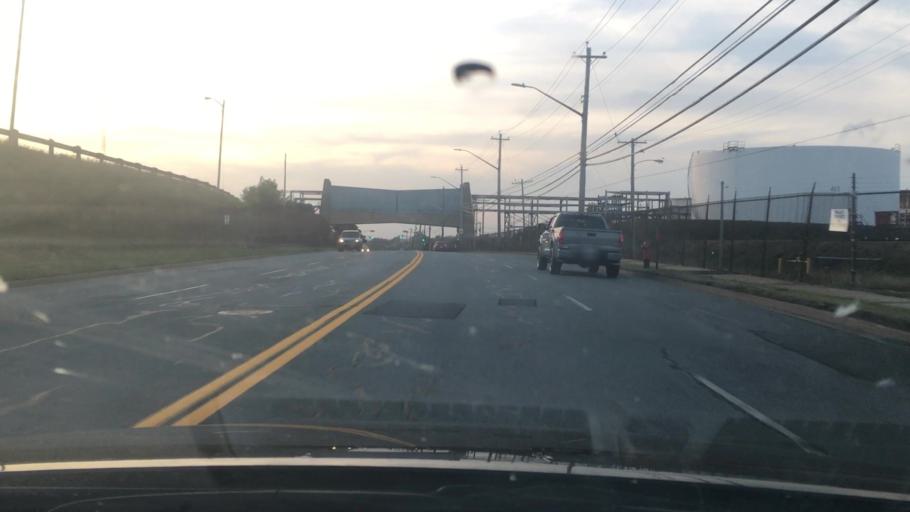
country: CA
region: Nova Scotia
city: Halifax
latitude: 44.6399
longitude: -63.5321
